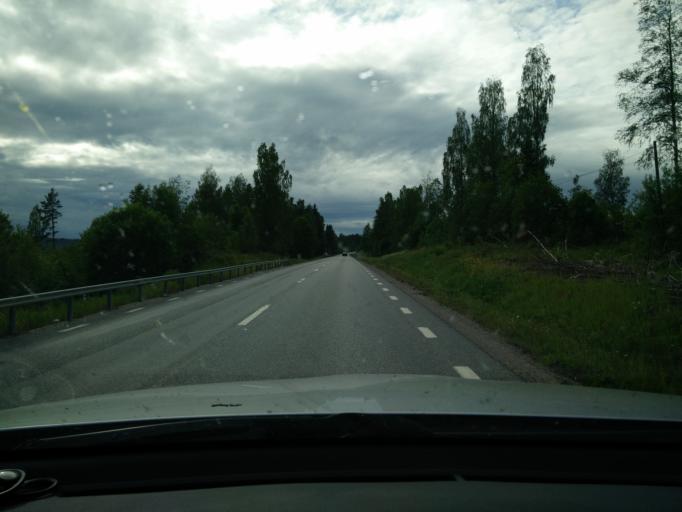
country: SE
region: Gaevleborg
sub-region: Nordanstigs Kommun
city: Bergsjoe
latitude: 62.0862
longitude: 16.7908
